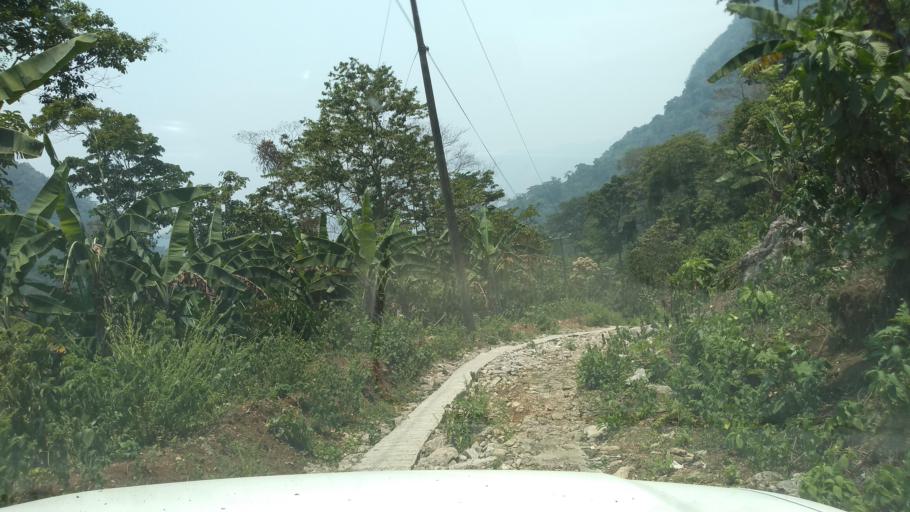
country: MX
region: Veracruz
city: Motzorongo
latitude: 18.6023
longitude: -96.7513
